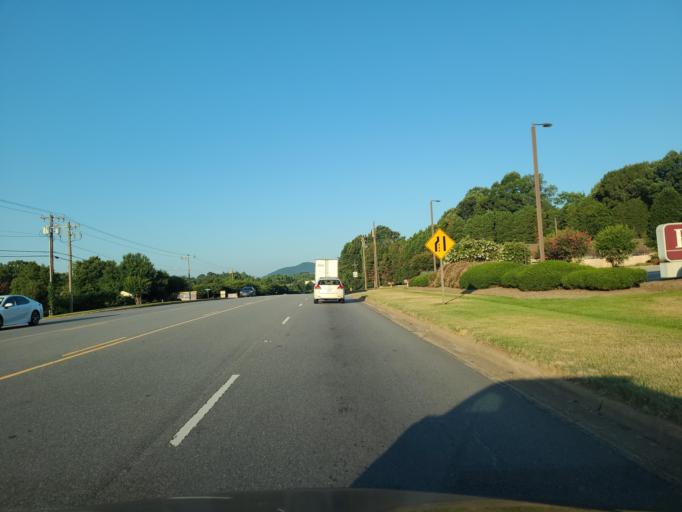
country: US
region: North Carolina
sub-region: Catawba County
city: Mountain View
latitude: 35.6904
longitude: -81.3592
